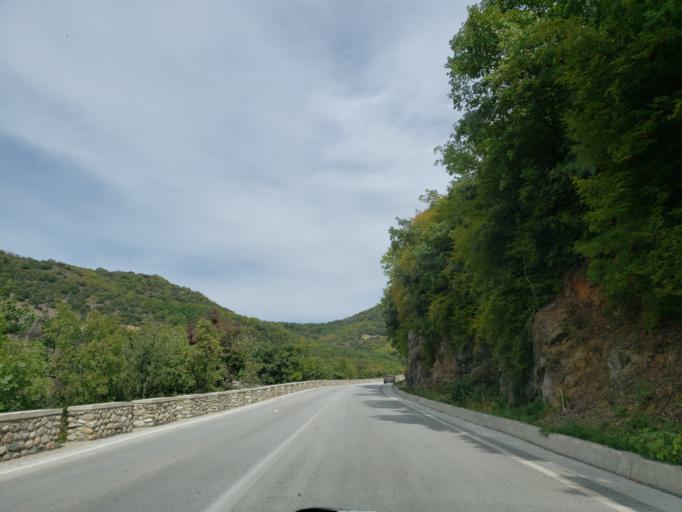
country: GR
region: Thessaly
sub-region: Trikala
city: Kastraki
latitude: 39.7231
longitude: 21.6336
